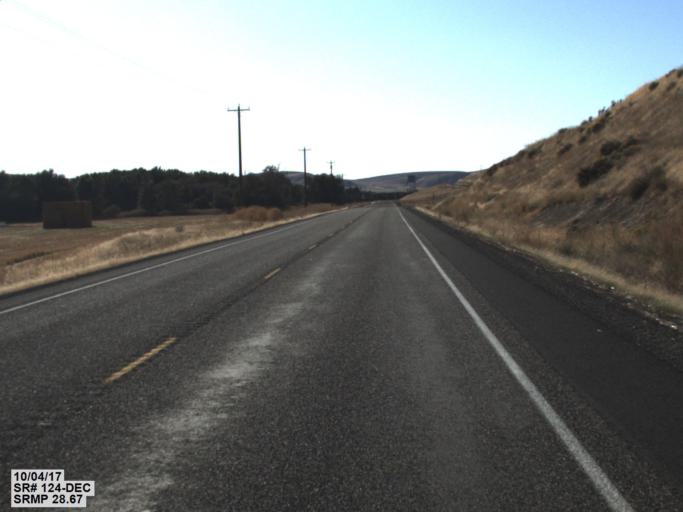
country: US
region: Washington
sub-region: Walla Walla County
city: Garrett
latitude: 46.2925
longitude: -118.4635
